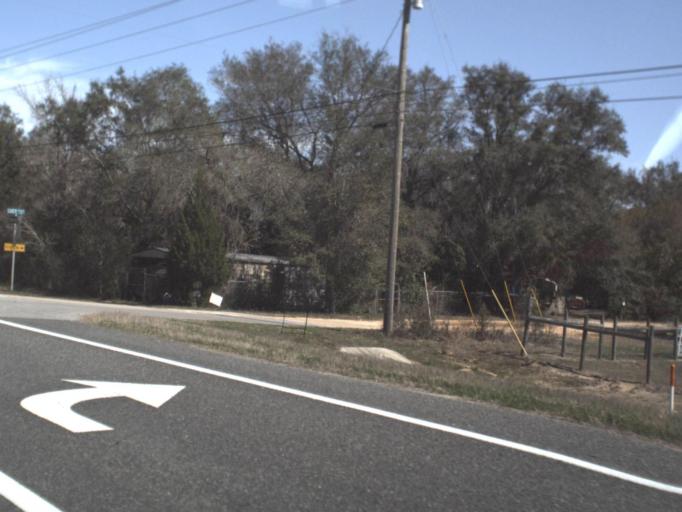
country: US
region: Florida
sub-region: Bay County
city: Lynn Haven
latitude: 30.4243
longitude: -85.6878
